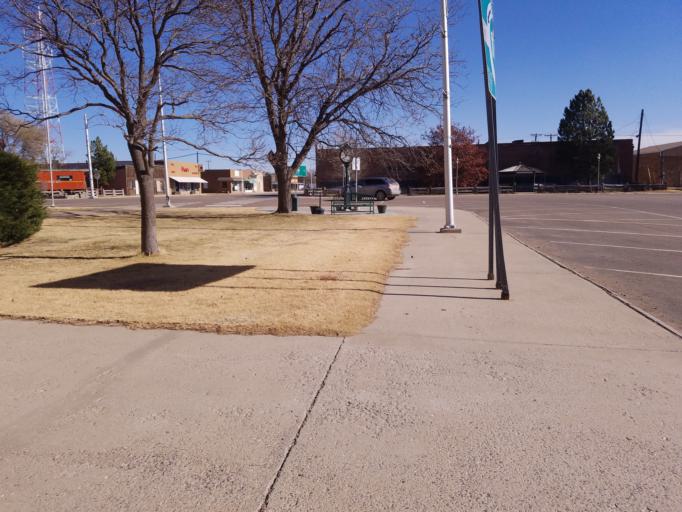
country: US
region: Oklahoma
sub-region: Cimarron County
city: Boise City
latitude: 36.7294
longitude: -102.5132
